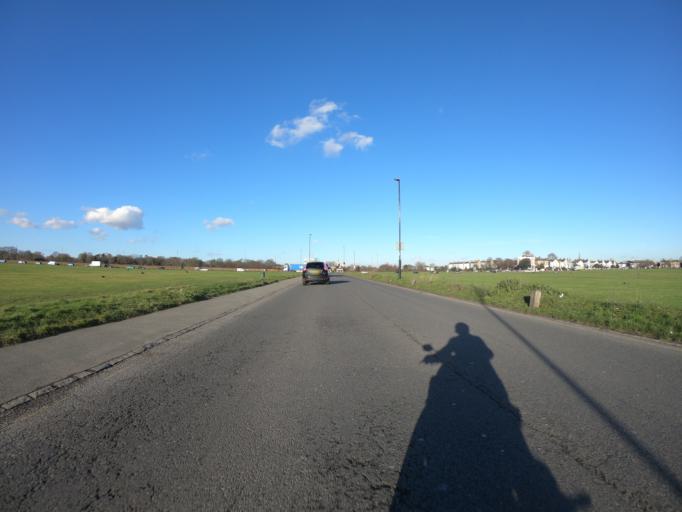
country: GB
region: England
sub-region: Greater London
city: Blackheath
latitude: 51.4713
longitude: 0.0092
